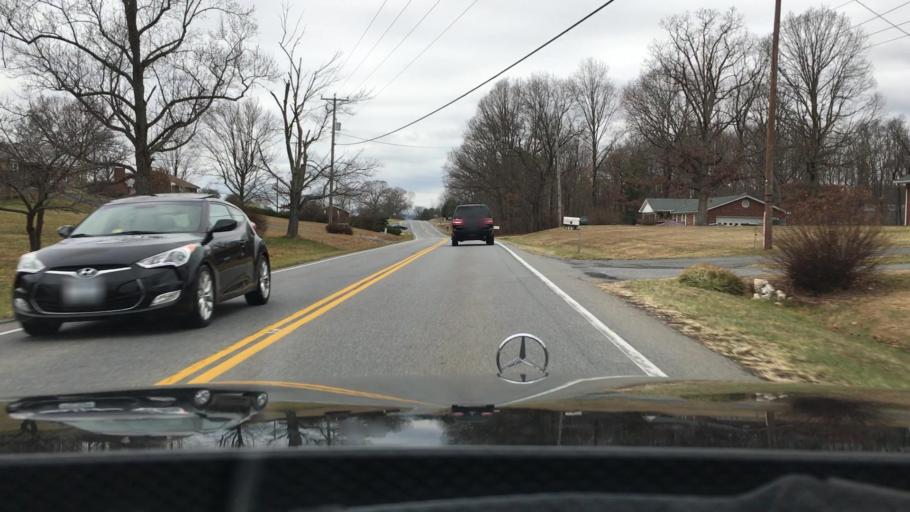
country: US
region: Virginia
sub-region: Botetourt County
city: Blue Ridge
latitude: 37.2518
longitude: -79.7008
